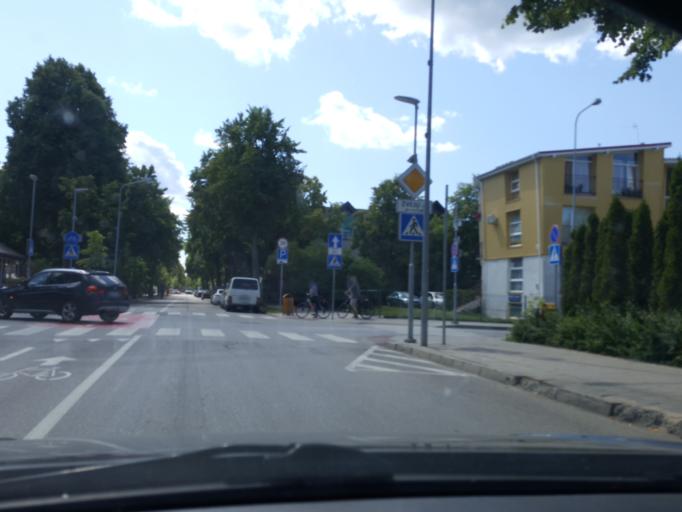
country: LT
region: Klaipedos apskritis
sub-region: Klaipeda
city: Palanga
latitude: 55.9254
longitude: 21.0710
